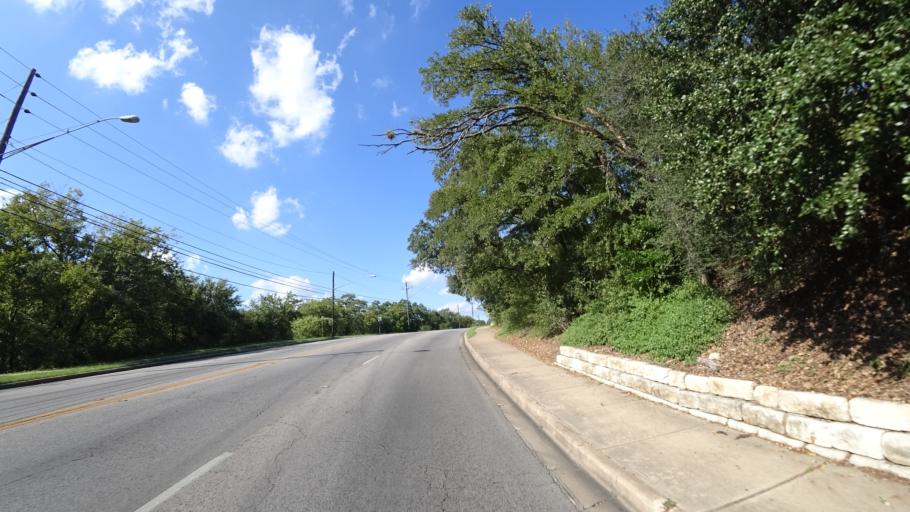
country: US
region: Texas
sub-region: Travis County
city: Austin
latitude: 30.2968
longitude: -97.7489
